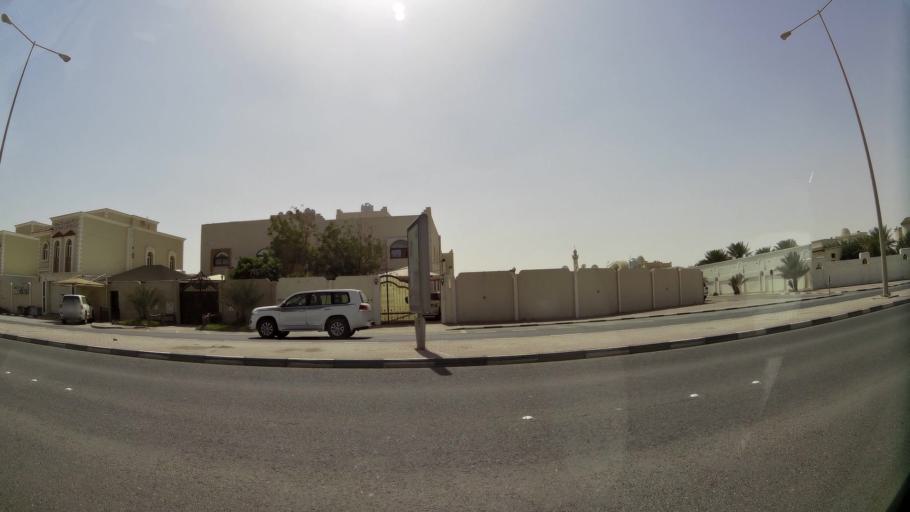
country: QA
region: Baladiyat Umm Salal
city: Umm Salal Muhammad
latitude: 25.3742
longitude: 51.4324
